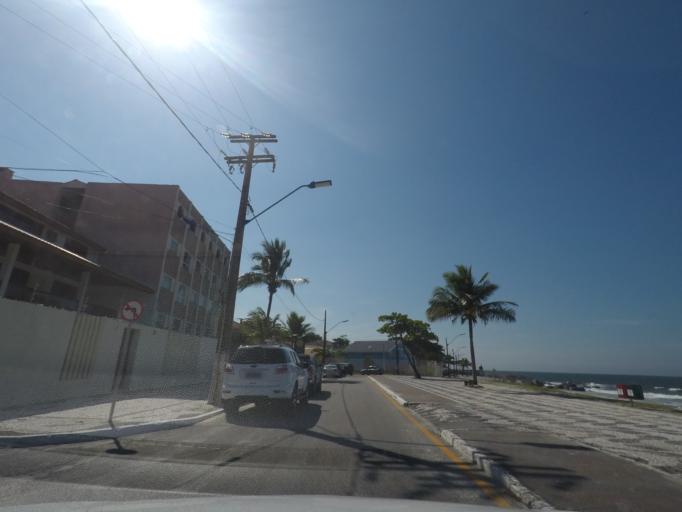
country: BR
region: Parana
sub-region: Guaratuba
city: Guaratuba
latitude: -25.8199
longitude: -48.5309
